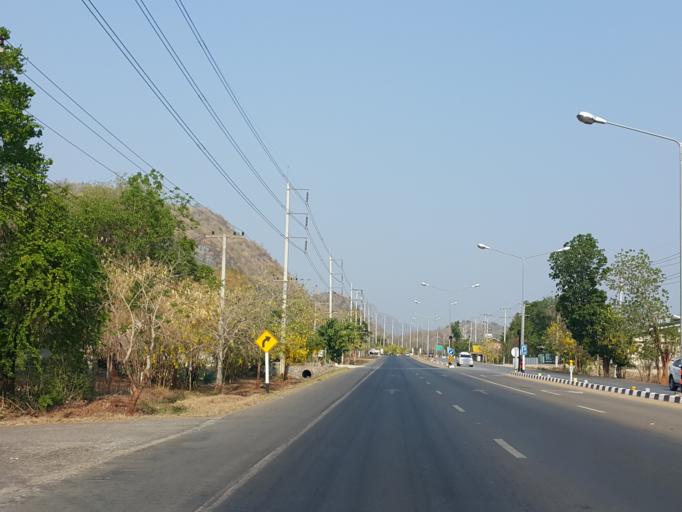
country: TH
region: Kanchanaburi
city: Kanchanaburi
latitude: 14.0690
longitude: 99.4019
